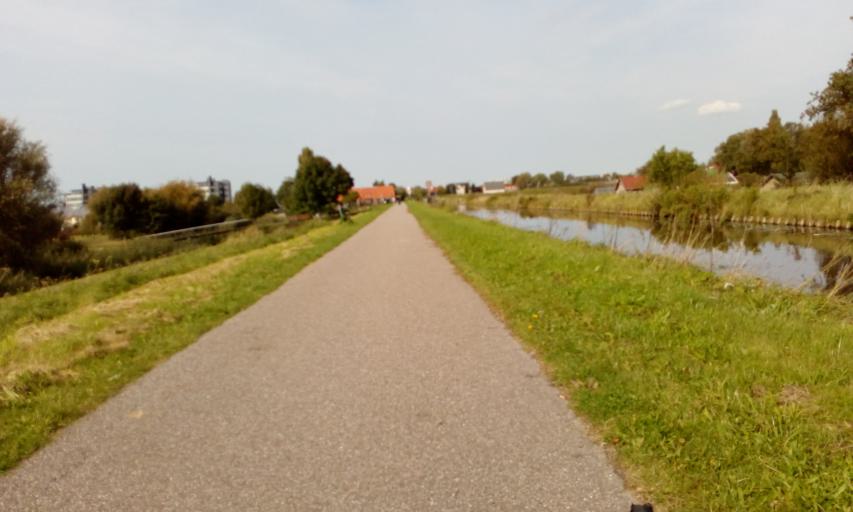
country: NL
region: South Holland
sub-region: Gemeente Rijswijk
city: Rijswijk
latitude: 52.0245
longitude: 4.3021
